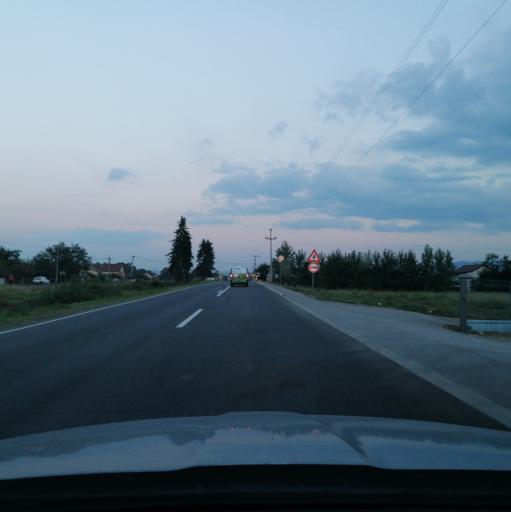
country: RS
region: Central Serbia
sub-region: Raski Okrug
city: Vrnjacka Banja
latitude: 43.6679
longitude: 20.8428
